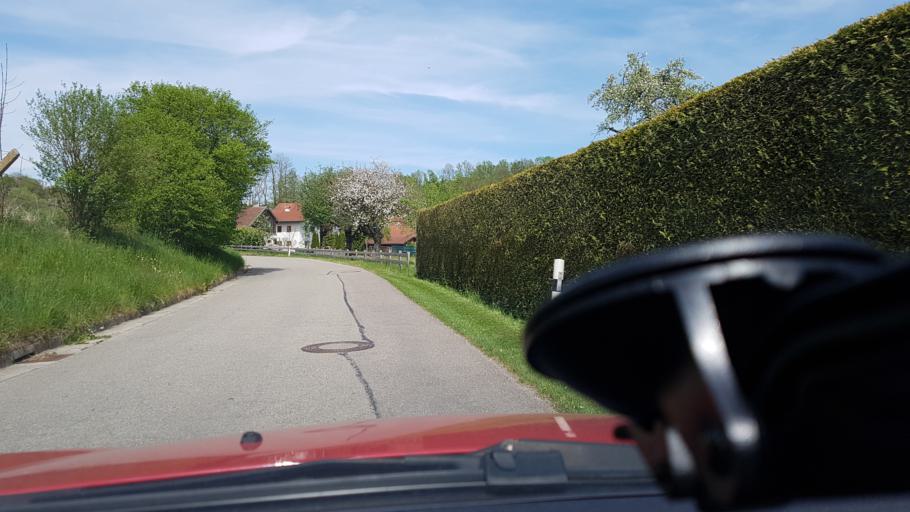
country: DE
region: Bavaria
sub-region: Lower Bavaria
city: Ering
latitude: 48.3104
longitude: 13.1383
